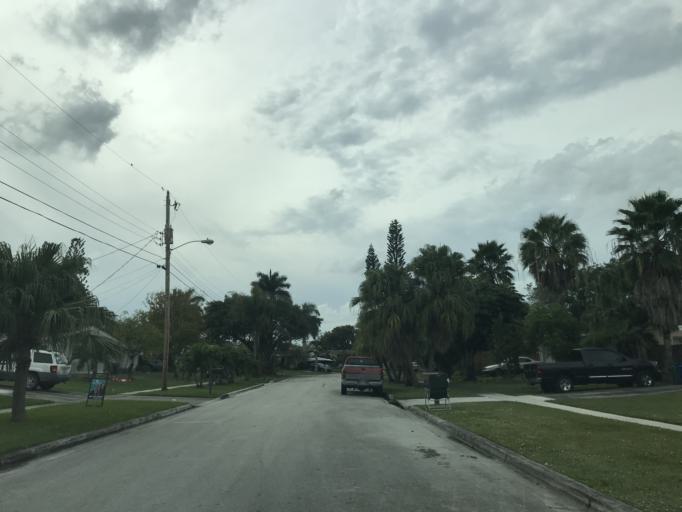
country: US
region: Florida
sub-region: Broward County
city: Margate
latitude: 26.2517
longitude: -80.2064
